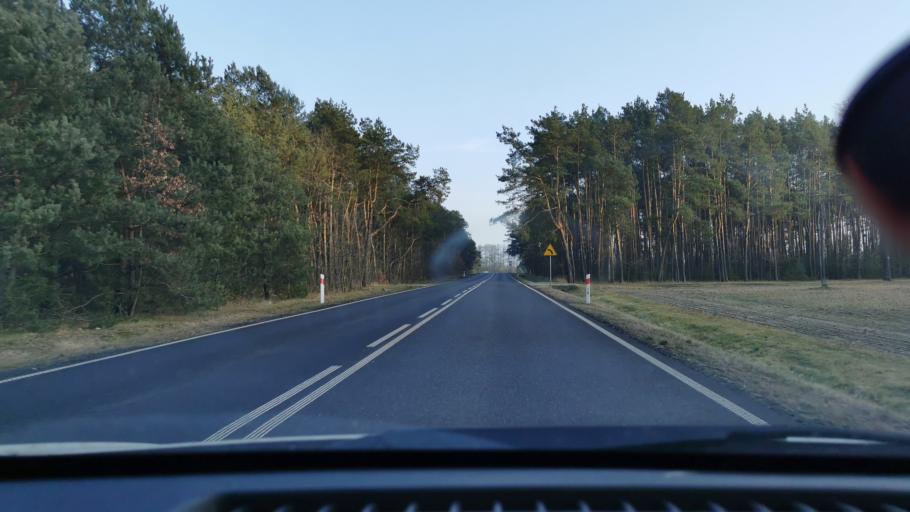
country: PL
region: Lodz Voivodeship
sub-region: Powiat pabianicki
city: Dlutow
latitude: 51.5145
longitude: 19.3283
